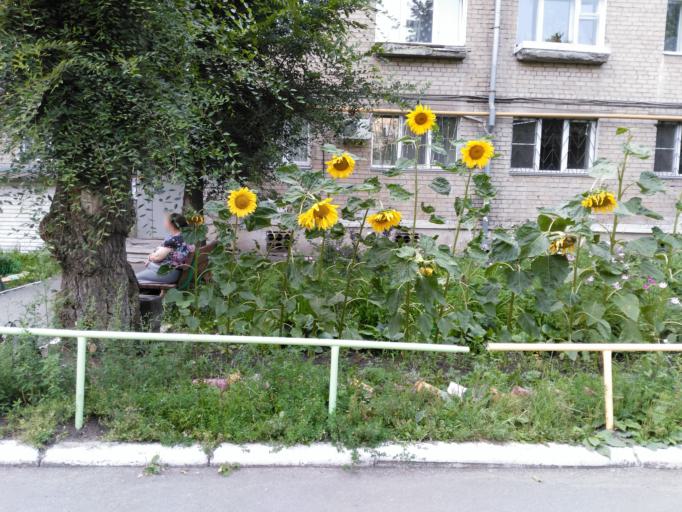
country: RU
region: Chelyabinsk
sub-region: Gorod Chelyabinsk
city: Chelyabinsk
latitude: 55.1544
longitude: 61.3952
